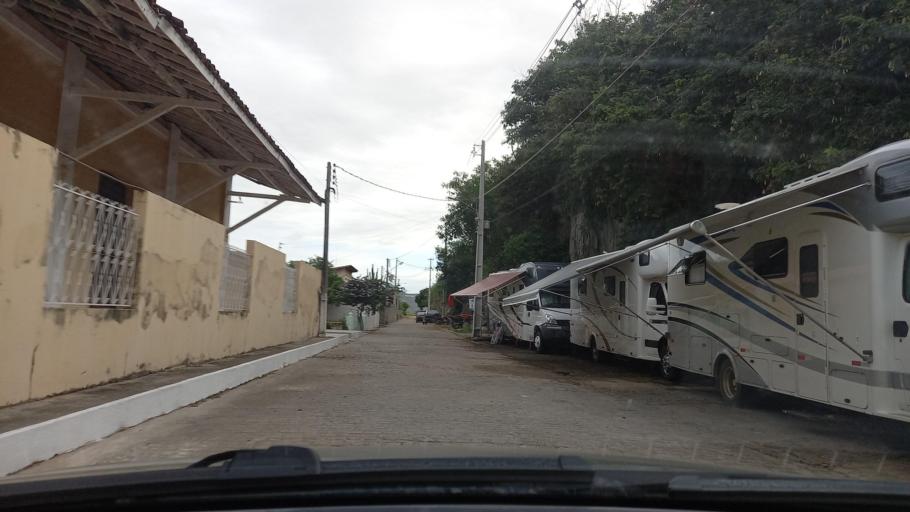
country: BR
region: Sergipe
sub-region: Caninde De Sao Francisco
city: Caninde de Sao Francisco
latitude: -9.6258
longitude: -37.7555
